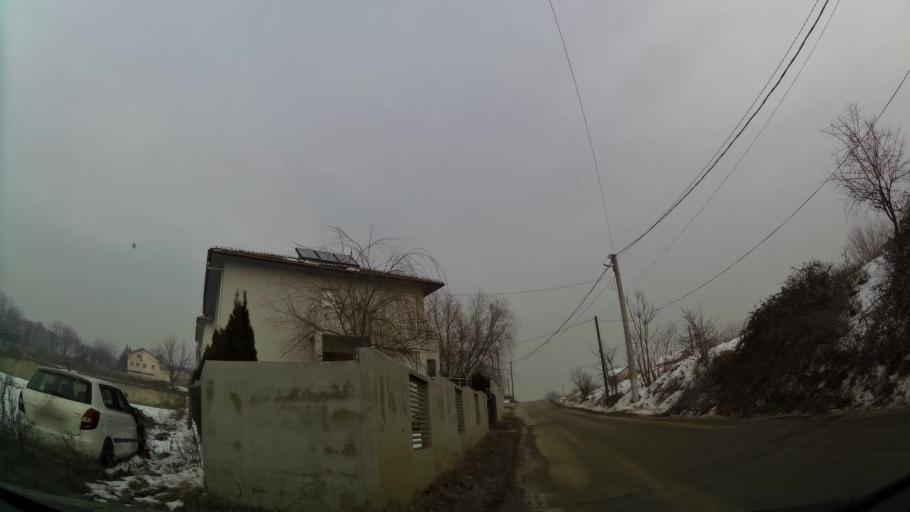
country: MK
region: Suto Orizari
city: Suto Orizare
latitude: 42.0273
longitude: 21.4106
